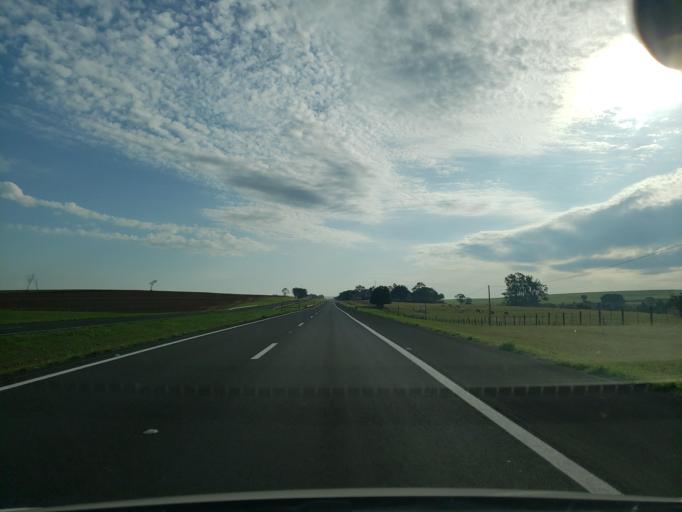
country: BR
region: Sao Paulo
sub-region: Valparaiso
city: Valparaiso
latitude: -21.2062
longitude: -50.7716
